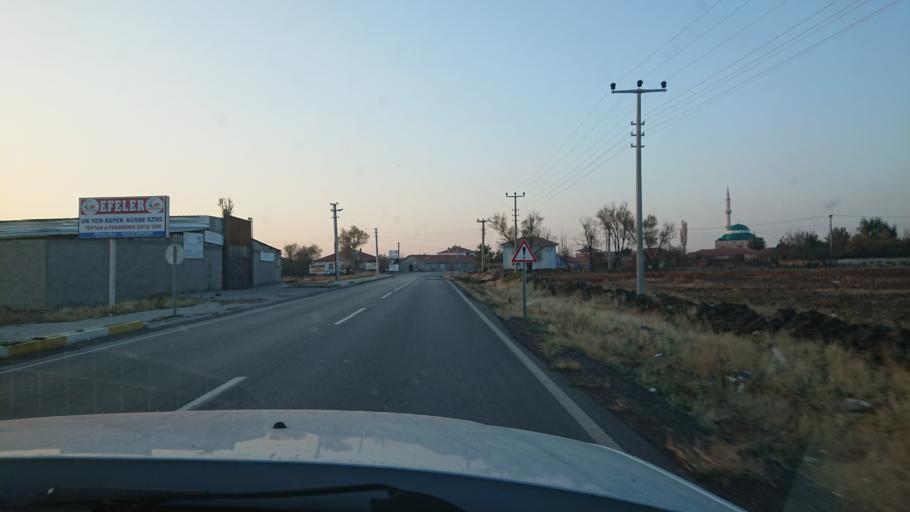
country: TR
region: Aksaray
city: Aksaray
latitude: 38.3127
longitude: 34.0613
